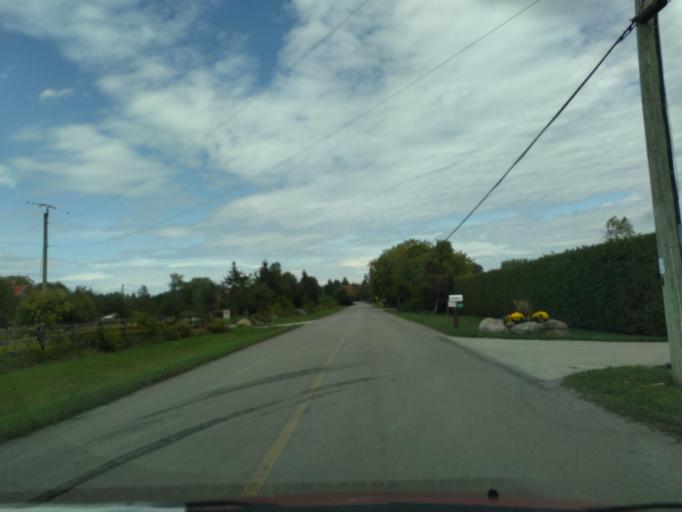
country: CA
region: Ontario
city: Keswick
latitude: 44.2685
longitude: -79.3659
